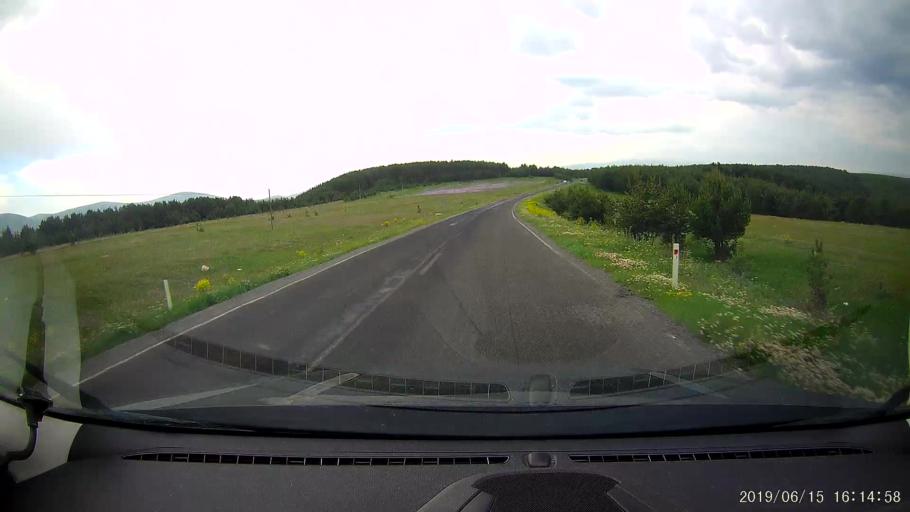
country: TR
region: Ardahan
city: Hanak
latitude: 41.2736
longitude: 42.8515
